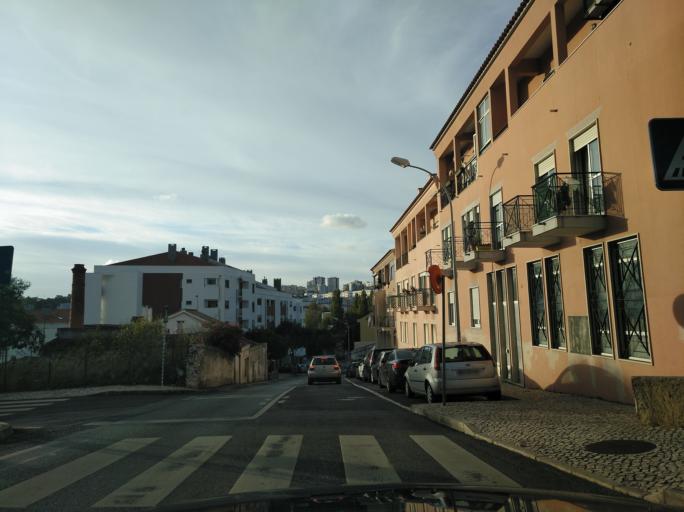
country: PT
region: Lisbon
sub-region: Oeiras
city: Alges
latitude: 38.7215
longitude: -9.2220
